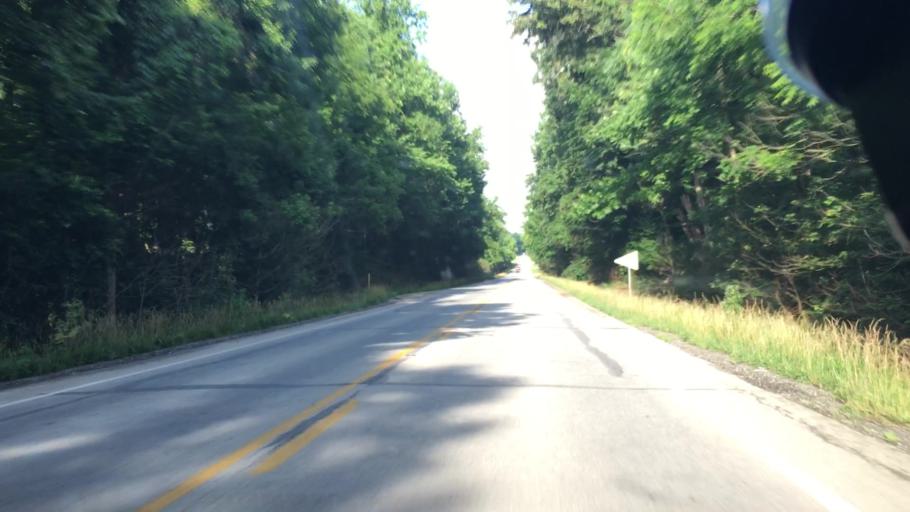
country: US
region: Kentucky
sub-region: Hancock County
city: Lewisport
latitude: 38.0014
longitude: -86.8426
